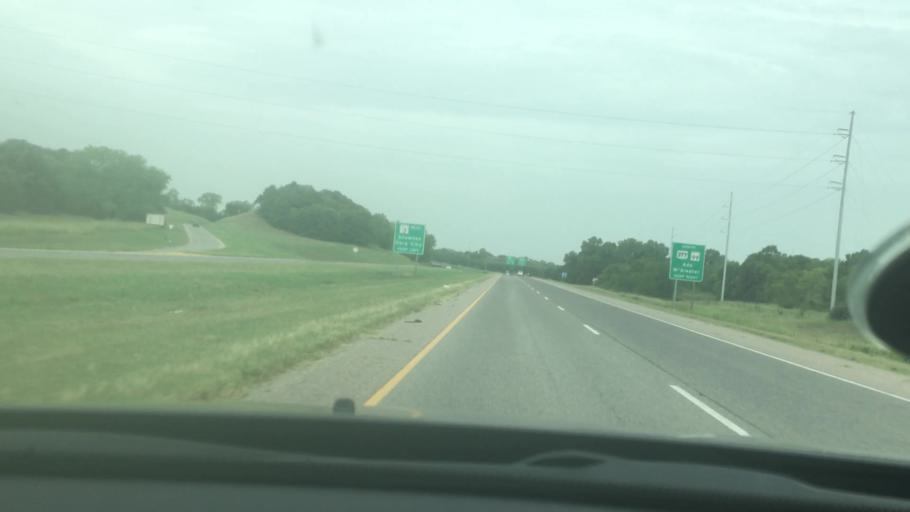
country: US
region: Oklahoma
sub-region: Pontotoc County
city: Ada
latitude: 34.7448
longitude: -96.6506
